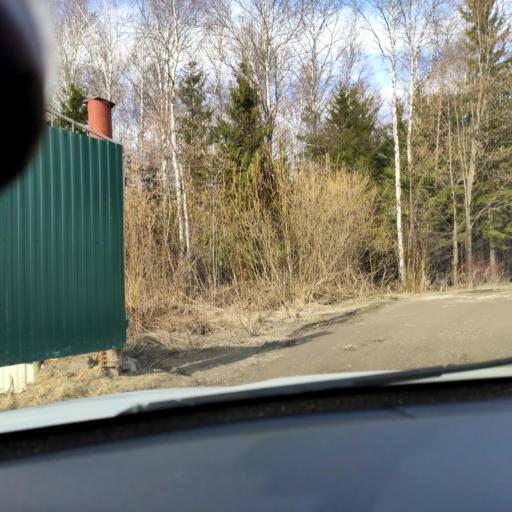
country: RU
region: Perm
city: Overyata
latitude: 58.0597
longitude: 55.9868
